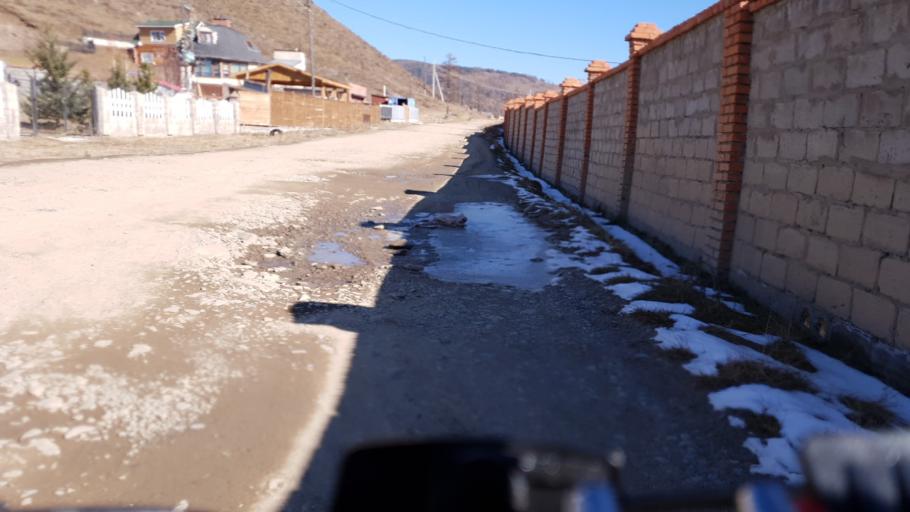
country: MN
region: Ulaanbaatar
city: Ulaanbaatar
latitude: 48.1161
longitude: 106.9251
